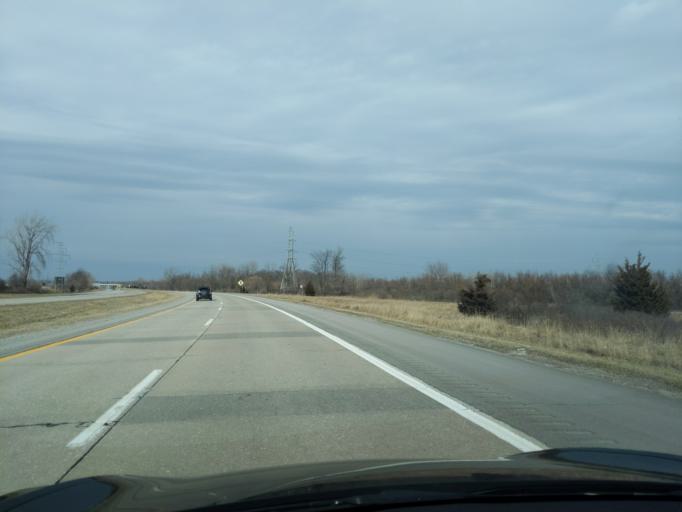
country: US
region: Michigan
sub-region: Bay County
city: Bay City
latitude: 43.6268
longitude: -83.9423
